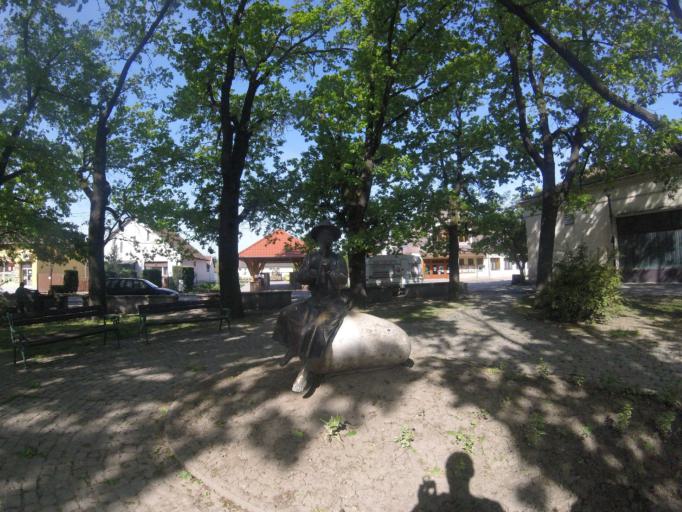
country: HU
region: Bekes
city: Doboz
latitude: 46.7360
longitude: 21.2436
